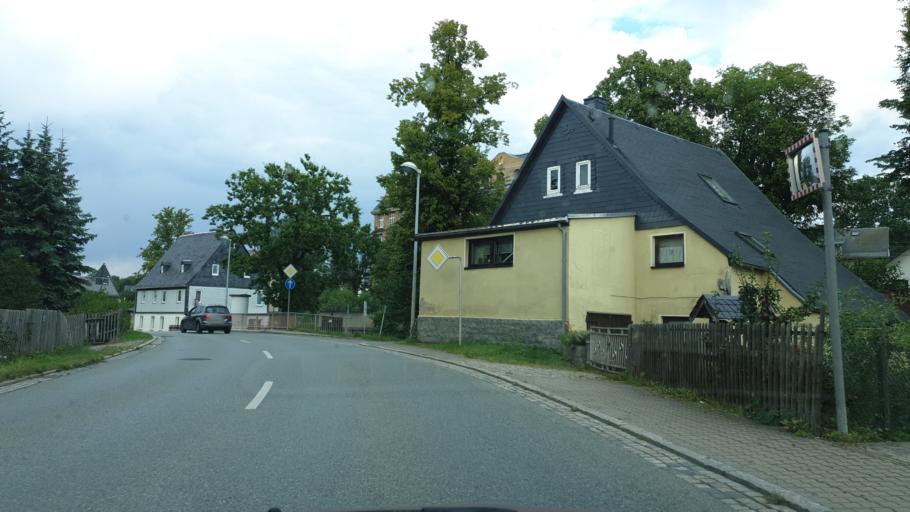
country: DE
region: Saxony
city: Zwonitz
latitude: 50.6335
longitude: 12.8134
